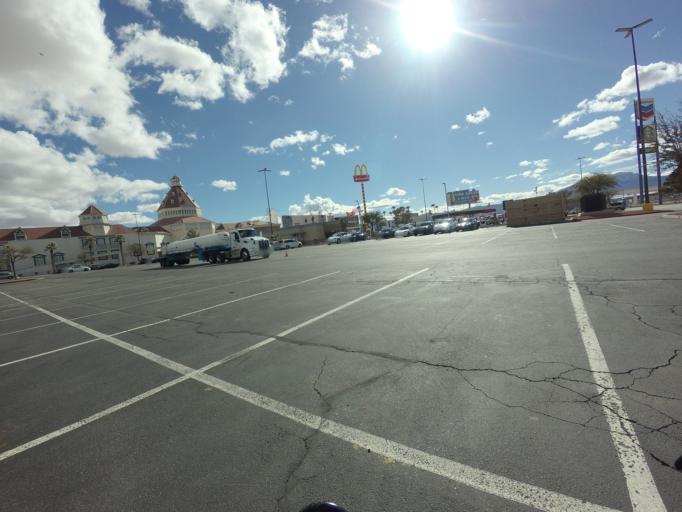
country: US
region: Nevada
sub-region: Clark County
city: Sandy Valley
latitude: 35.6110
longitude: -115.3878
